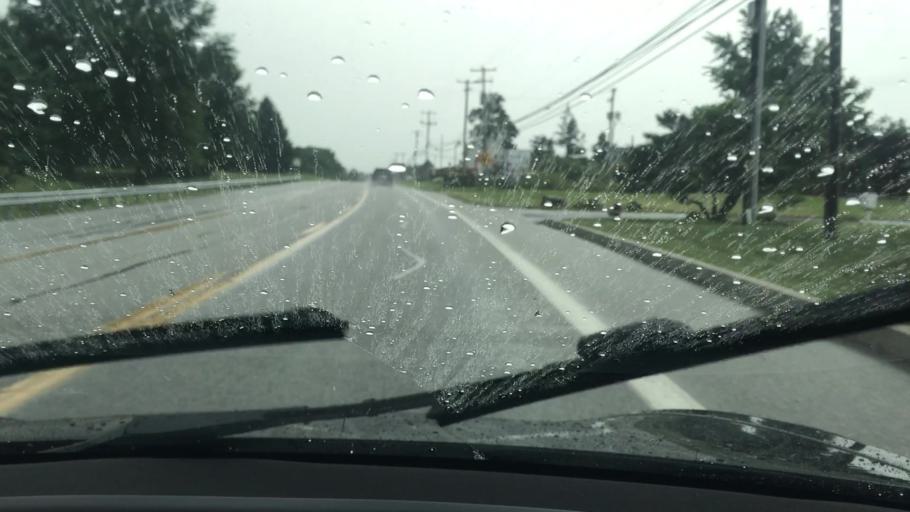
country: US
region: Pennsylvania
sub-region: Dauphin County
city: Lawrence Park
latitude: 40.3404
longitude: -76.8085
